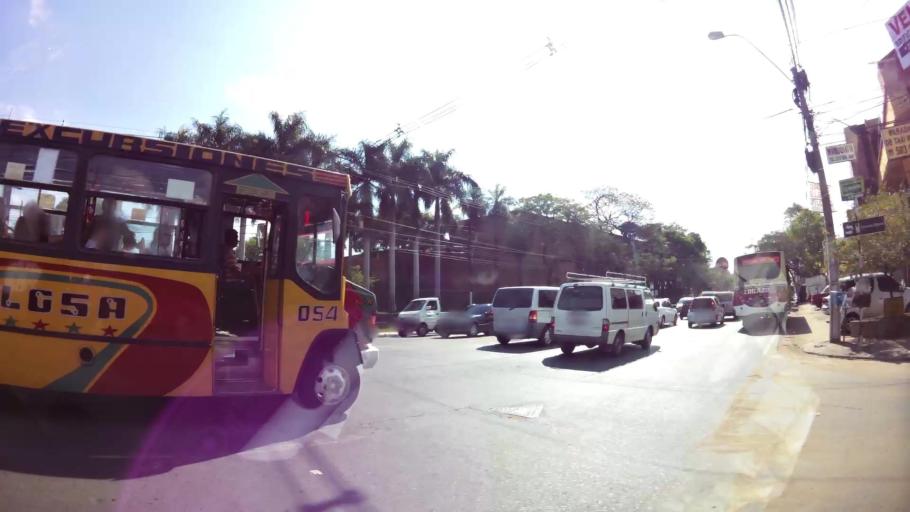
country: PY
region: Central
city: Fernando de la Mora
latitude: -25.3277
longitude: -57.5463
